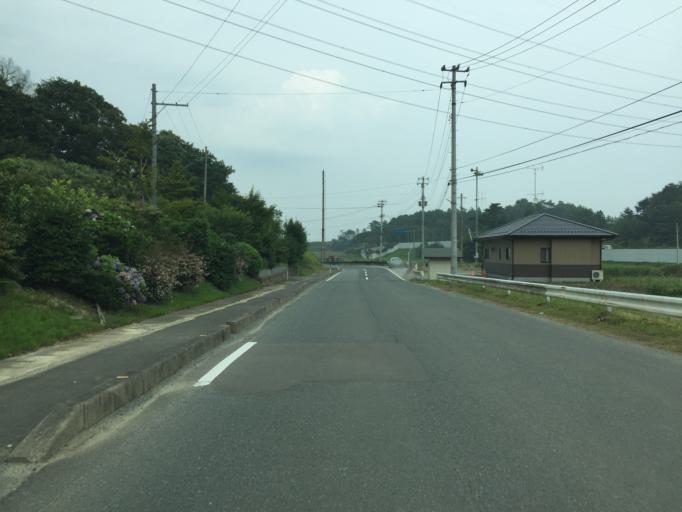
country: JP
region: Fukushima
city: Namie
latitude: 37.6522
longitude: 141.0138
